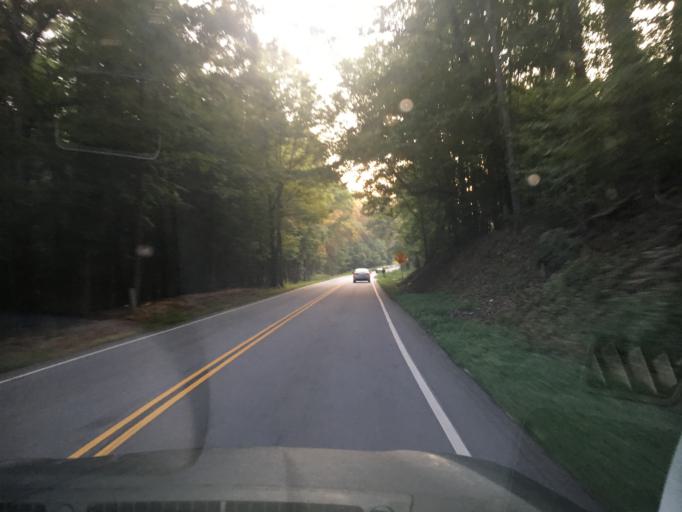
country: US
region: South Carolina
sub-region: Spartanburg County
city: Duncan
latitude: 34.8854
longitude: -82.1221
